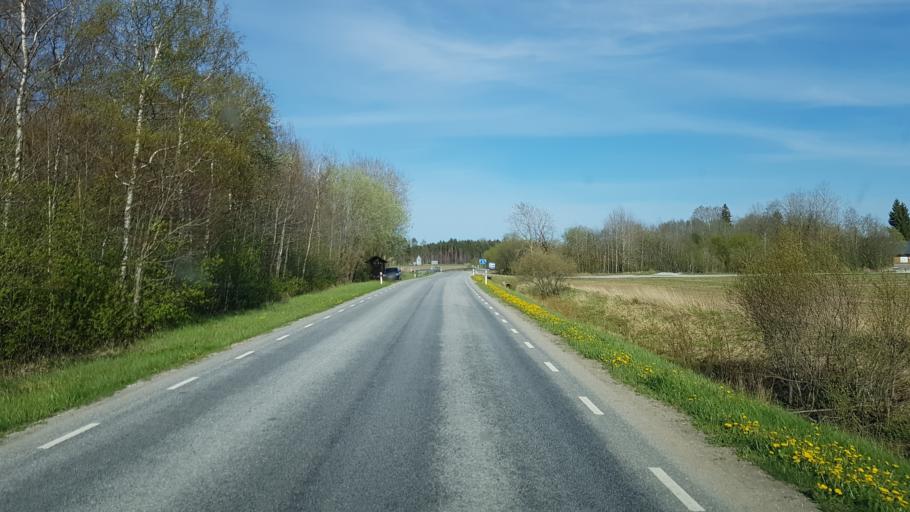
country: EE
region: Harju
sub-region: Saue linn
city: Saue
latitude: 59.3376
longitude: 24.5810
